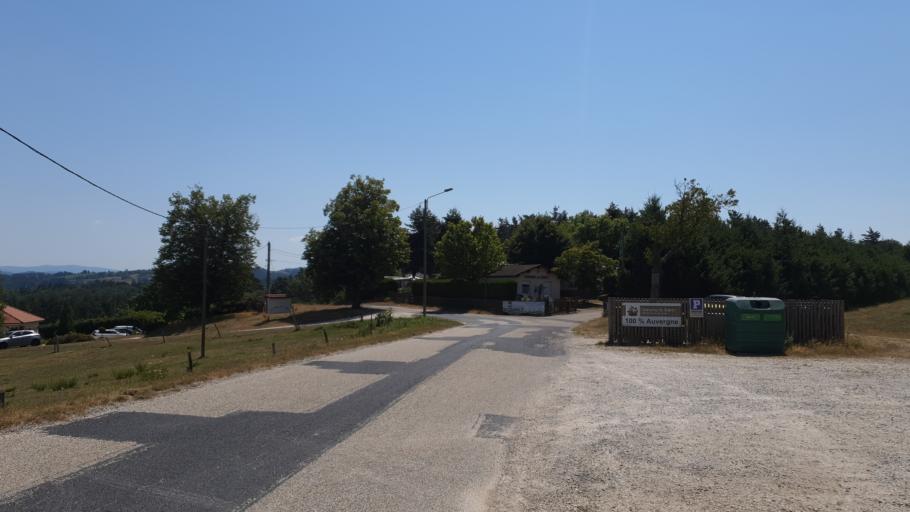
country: FR
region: Auvergne
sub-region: Departement de la Haute-Loire
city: Saint-Maurice-de-Lignon
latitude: 45.2232
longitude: 4.1511
